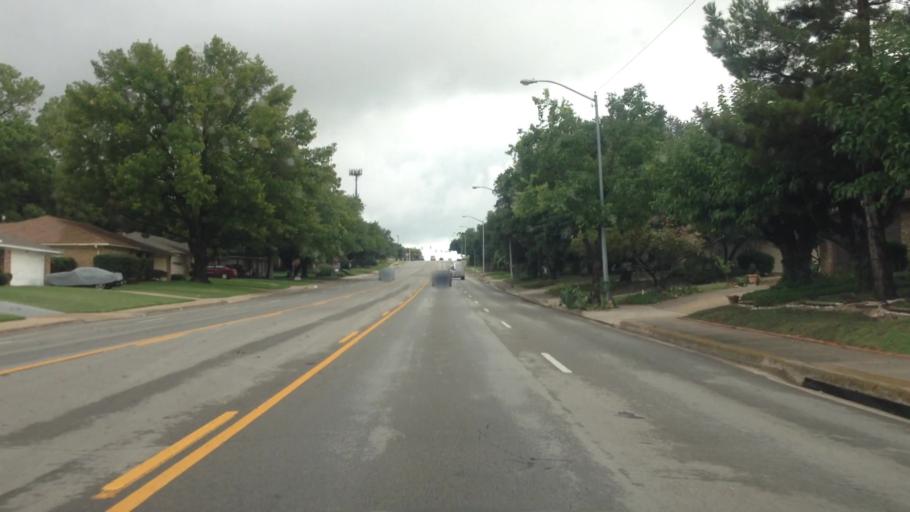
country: US
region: Texas
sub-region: Tarrant County
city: Edgecliff Village
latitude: 32.6520
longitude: -97.3960
